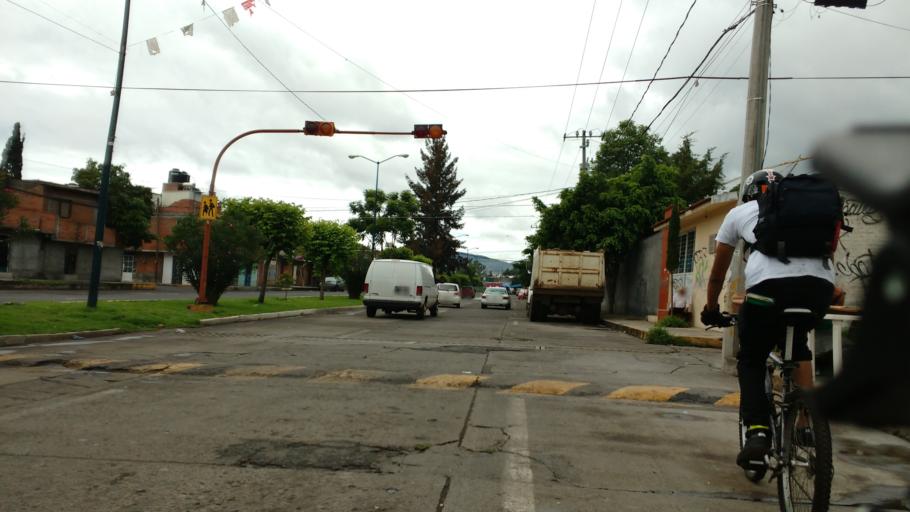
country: MX
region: Michoacan
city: Morelia
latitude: 19.7126
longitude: -101.2124
